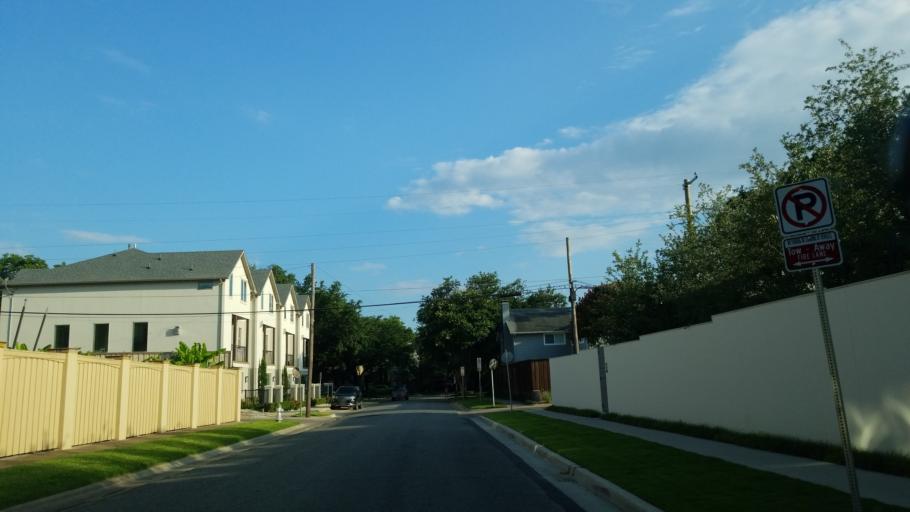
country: US
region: Texas
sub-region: Dallas County
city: Highland Park
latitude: 32.8448
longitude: -96.7900
